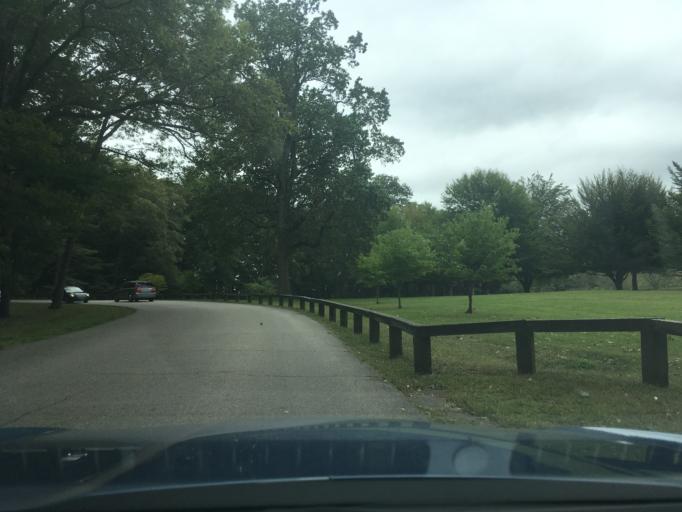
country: US
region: Rhode Island
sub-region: Kent County
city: East Greenwich
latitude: 41.6523
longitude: -71.4432
